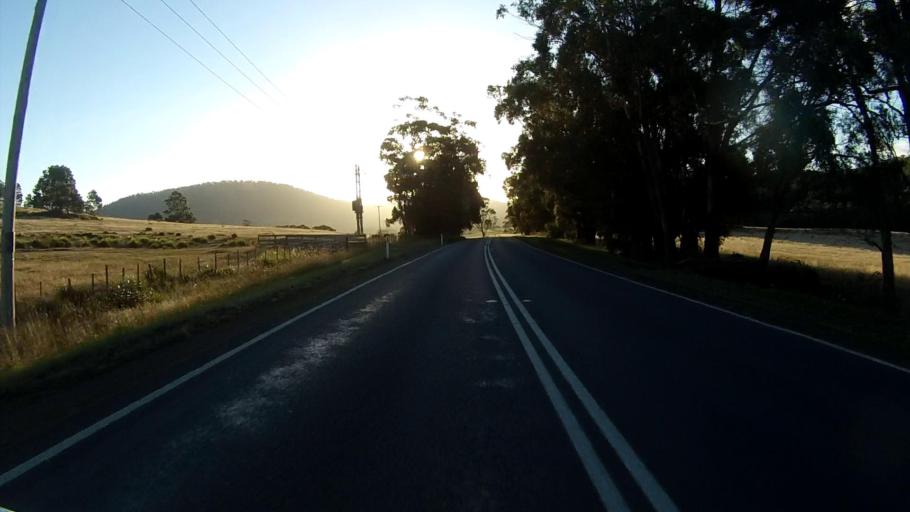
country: AU
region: Tasmania
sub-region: Sorell
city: Sorell
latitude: -42.8153
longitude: 147.7854
